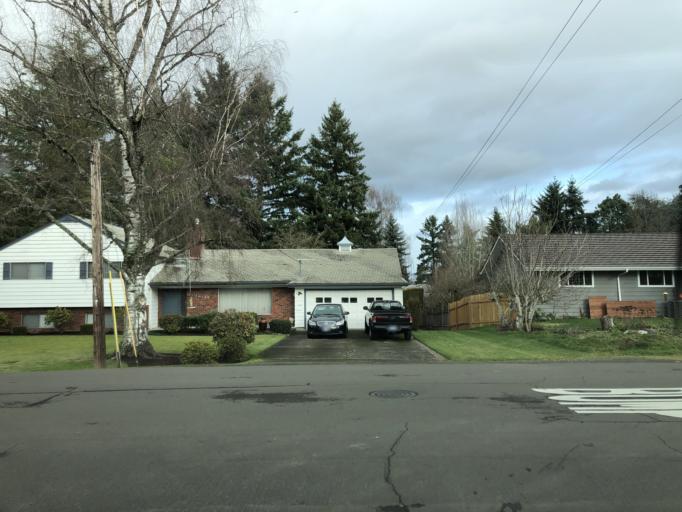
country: US
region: Oregon
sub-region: Washington County
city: Tigard
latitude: 45.4240
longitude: -122.7875
